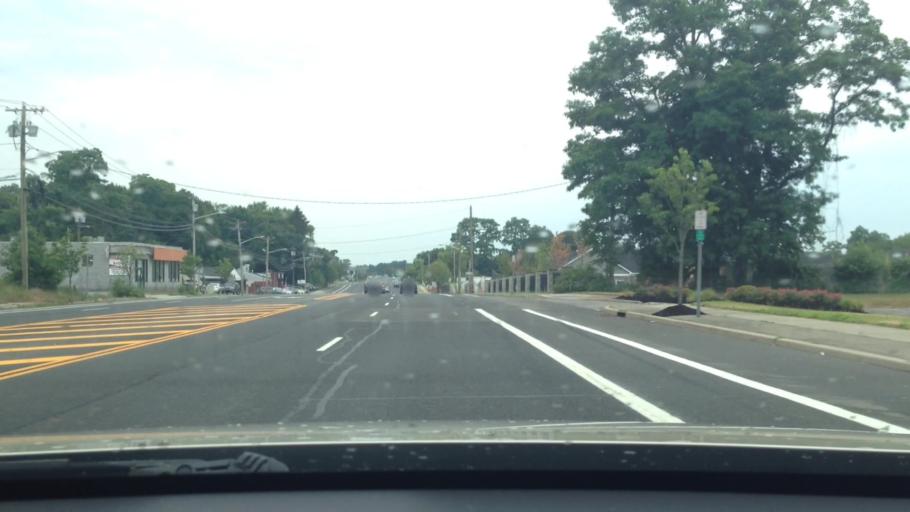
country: US
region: New York
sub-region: Suffolk County
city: Selden
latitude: 40.8676
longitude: -73.0280
